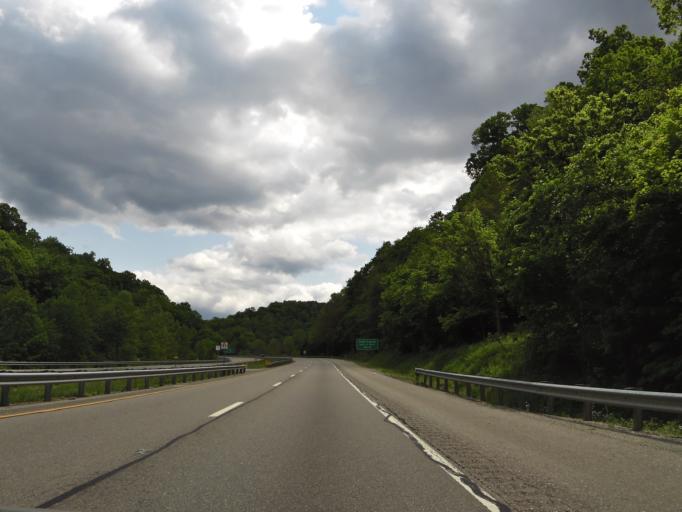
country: US
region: West Virginia
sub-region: Kanawha County
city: Charleston
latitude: 38.4074
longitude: -81.6237
